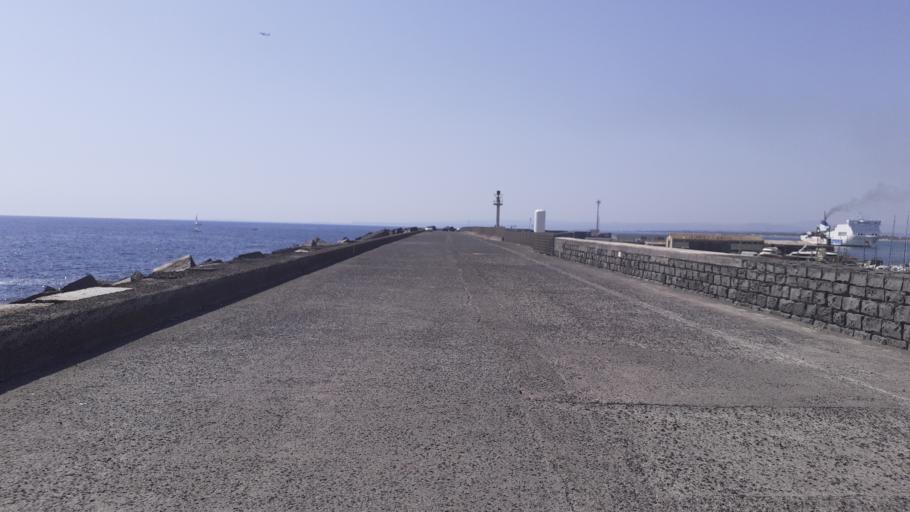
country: IT
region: Sicily
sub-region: Catania
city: Catania
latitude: 37.4936
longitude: 15.0998
